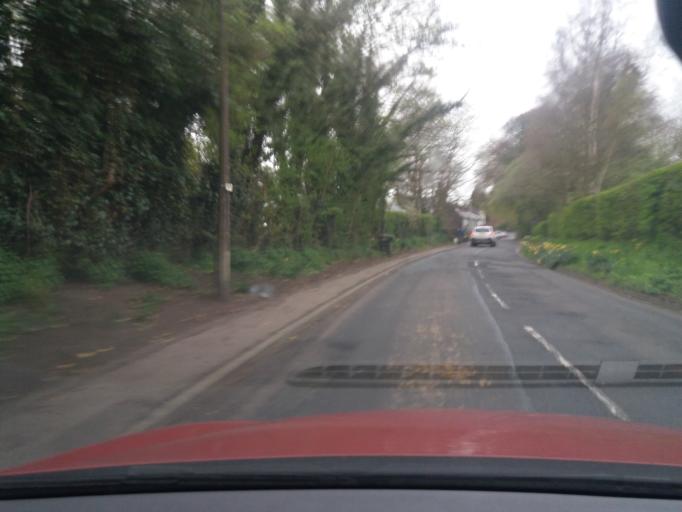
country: GB
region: England
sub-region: Lancashire
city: Clayton-le-Woods
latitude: 53.6848
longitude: -2.6355
